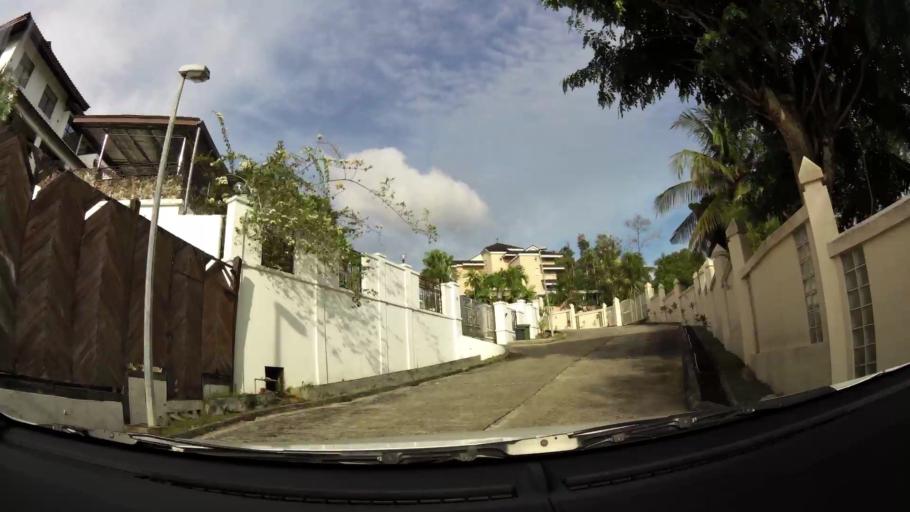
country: BN
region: Brunei and Muara
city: Bandar Seri Begawan
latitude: 4.9085
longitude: 114.8977
